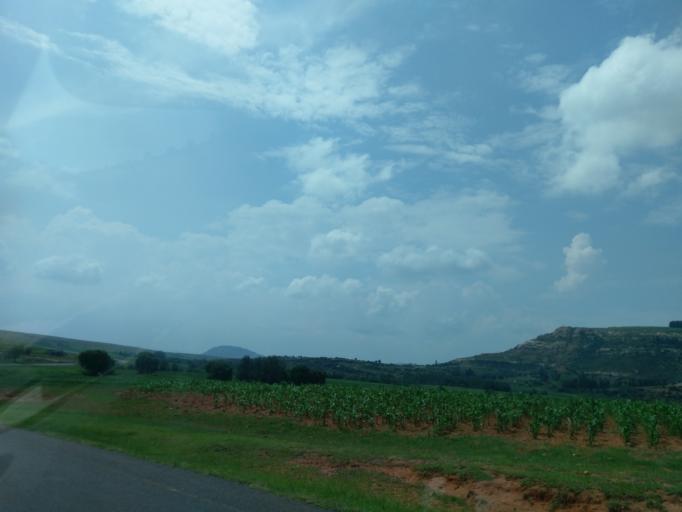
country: LS
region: Leribe
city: Leribe
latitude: -29.0121
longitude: 28.0004
